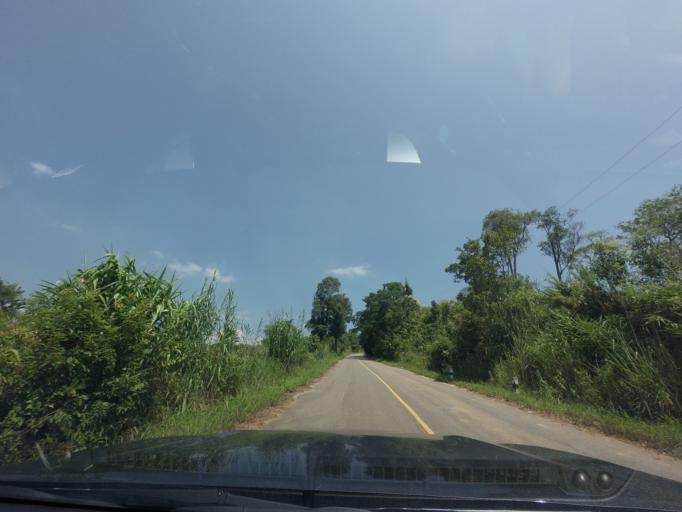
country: TH
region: Loei
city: Na Haeo
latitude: 17.5698
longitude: 100.8950
